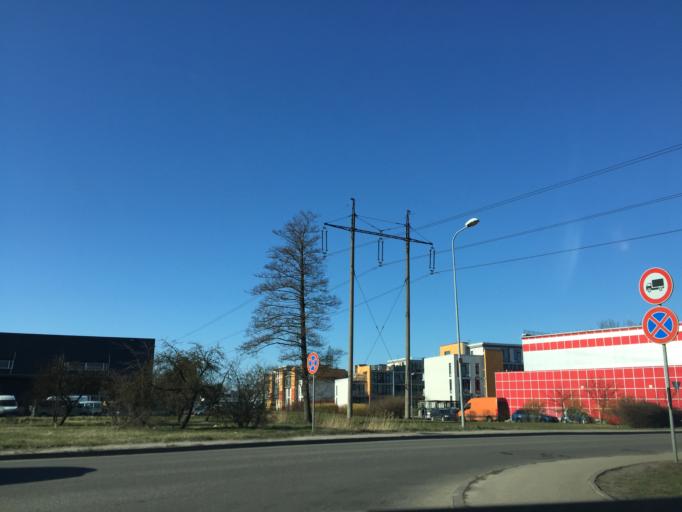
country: LV
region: Marupe
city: Marupe
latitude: 56.9396
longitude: 24.0035
